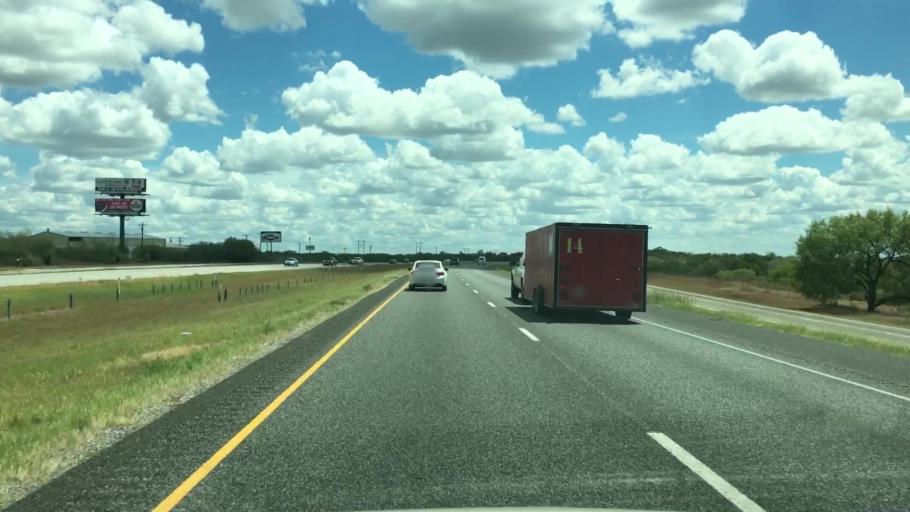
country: US
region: Texas
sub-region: Atascosa County
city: Pleasanton
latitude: 28.8880
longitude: -98.4068
